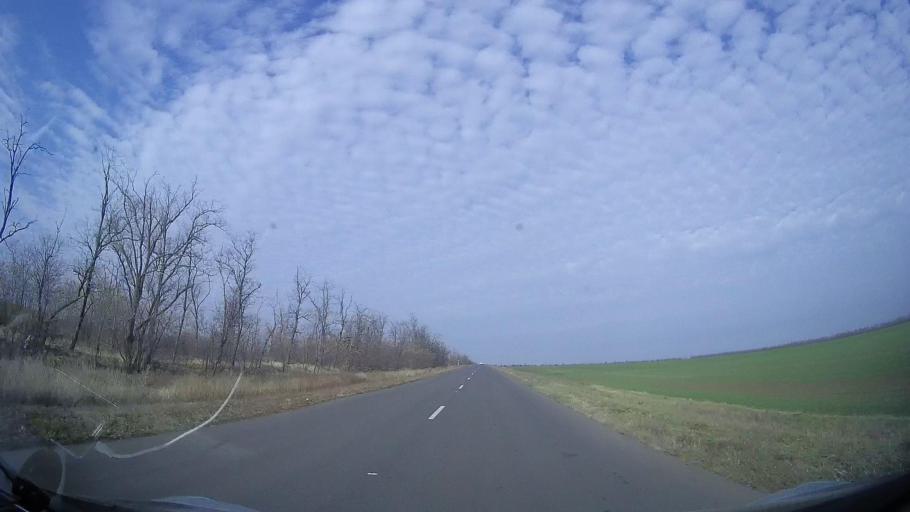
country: RU
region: Rostov
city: Gigant
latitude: 46.8510
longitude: 41.2846
